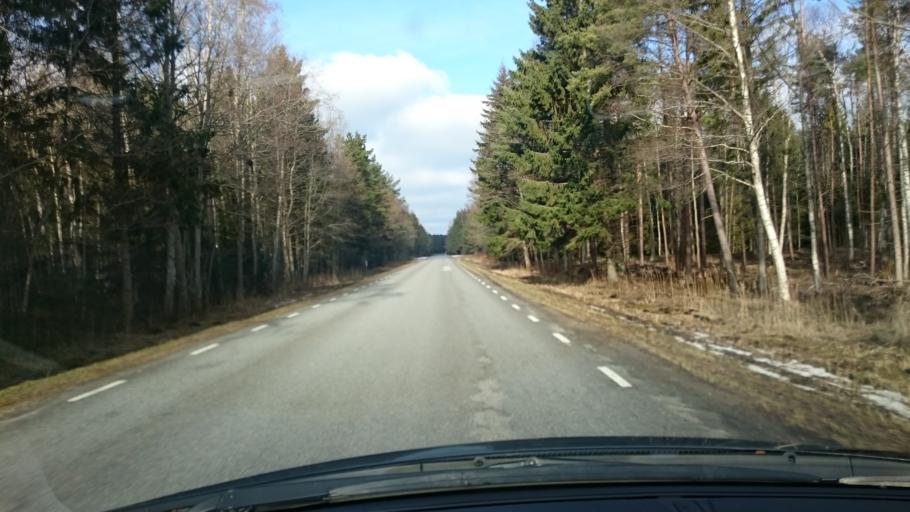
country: EE
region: Harju
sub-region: Keila linn
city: Keila
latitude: 59.3857
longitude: 24.2979
